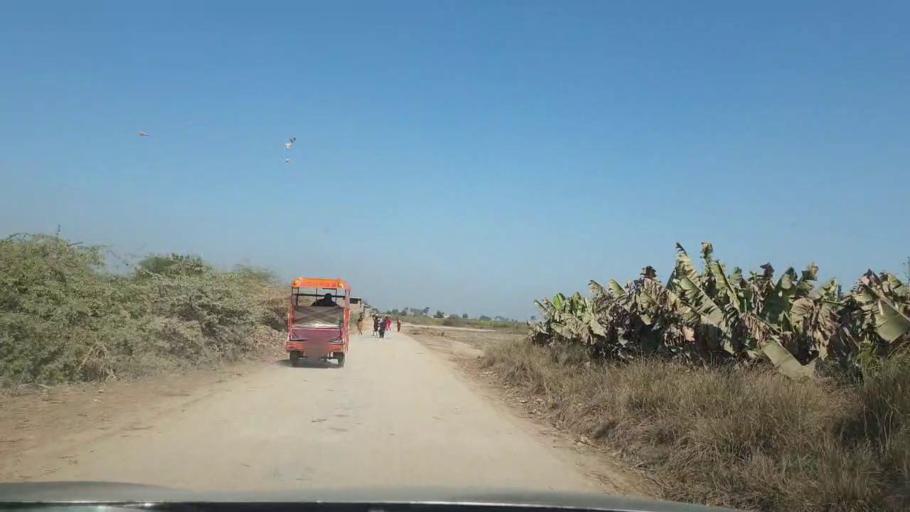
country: PK
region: Sindh
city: Tando Adam
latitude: 25.6294
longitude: 68.6662
